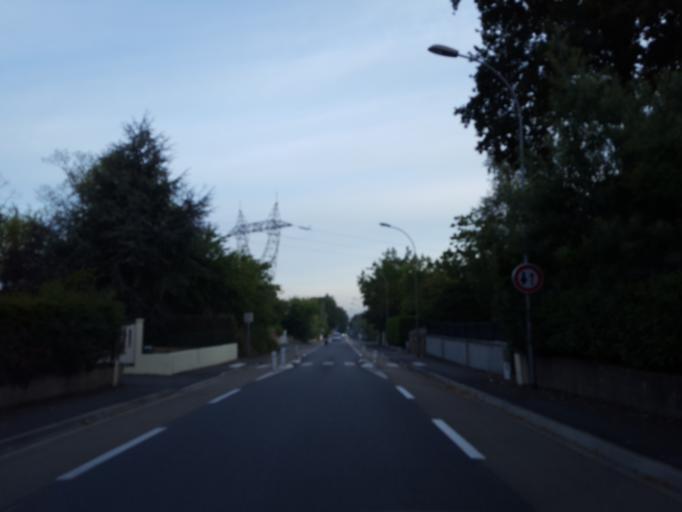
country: FR
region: Pays de la Loire
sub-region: Departement de la Loire-Atlantique
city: Basse-Goulaine
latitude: 47.1964
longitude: -1.4644
